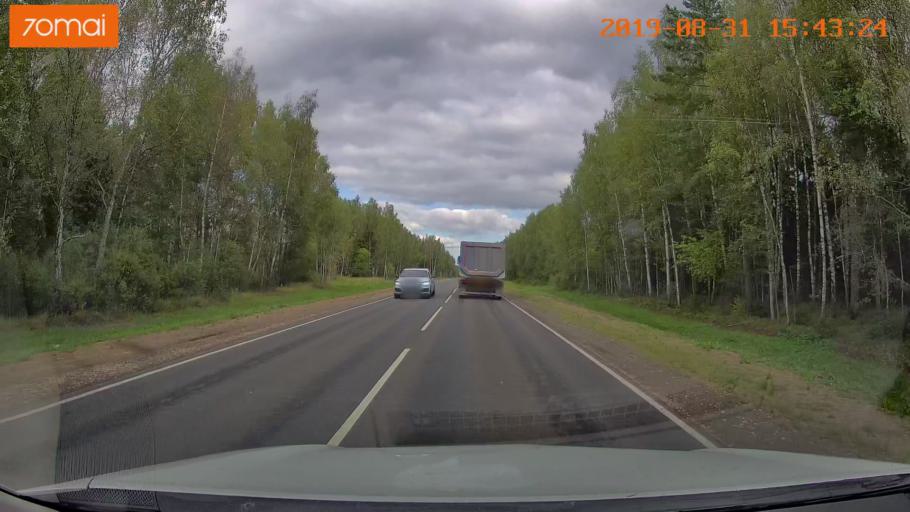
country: RU
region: Kaluga
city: Mosal'sk
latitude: 54.6528
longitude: 34.9100
